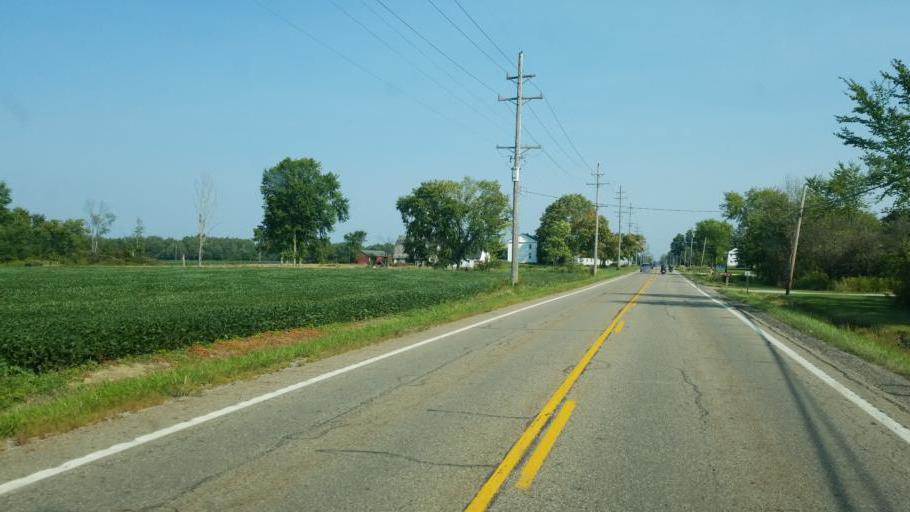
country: US
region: Ohio
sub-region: Ashtabula County
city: Orwell
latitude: 41.5872
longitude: -80.8651
